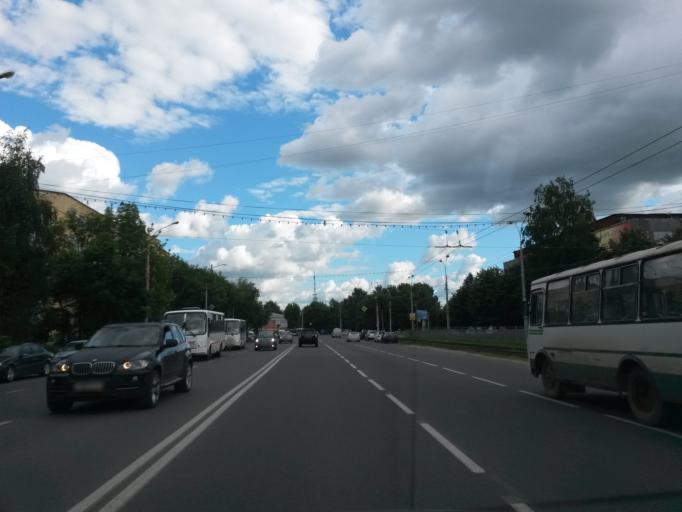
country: RU
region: Jaroslavl
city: Yaroslavl
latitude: 57.6388
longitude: 39.8581
